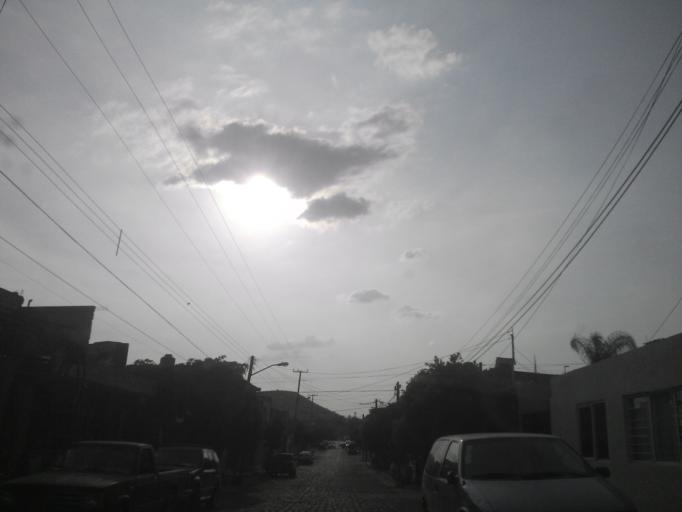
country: MX
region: Jalisco
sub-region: Tlajomulco de Zuniga
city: Altus Bosques
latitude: 20.6083
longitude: -103.3790
